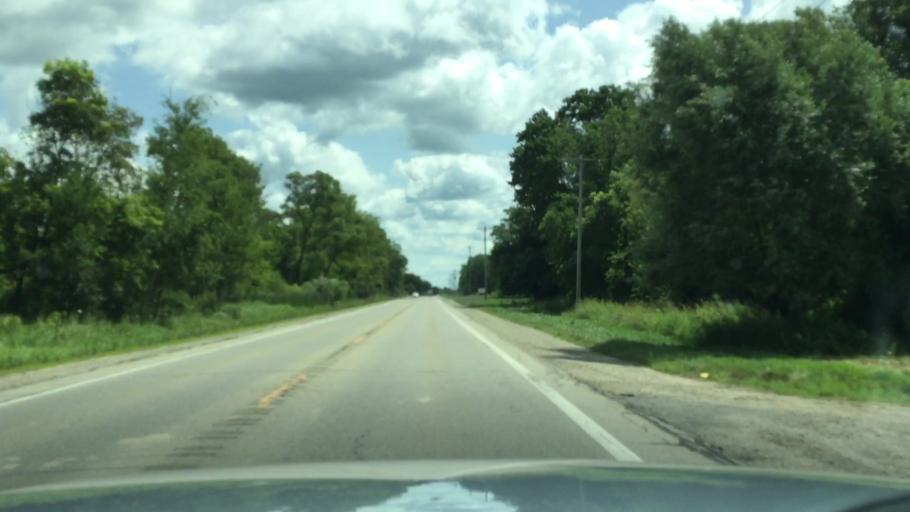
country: US
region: Michigan
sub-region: Montcalm County
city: Greenville
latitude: 43.1706
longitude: -85.2206
